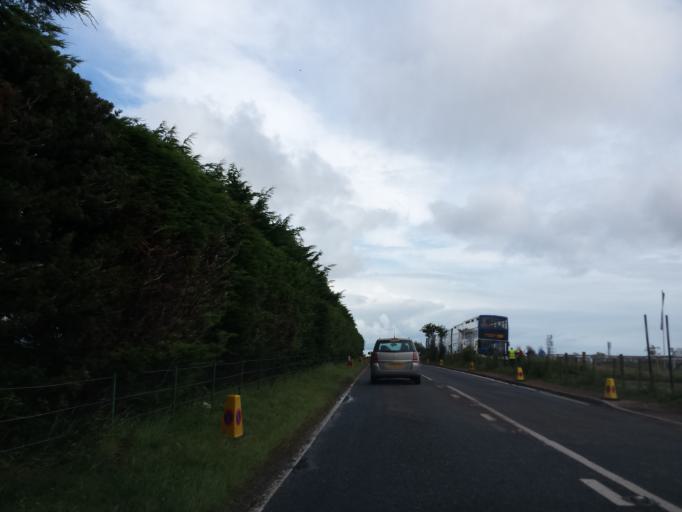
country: GB
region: Scotland
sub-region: Fife
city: Saint Andrews
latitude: 56.3240
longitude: -2.8124
